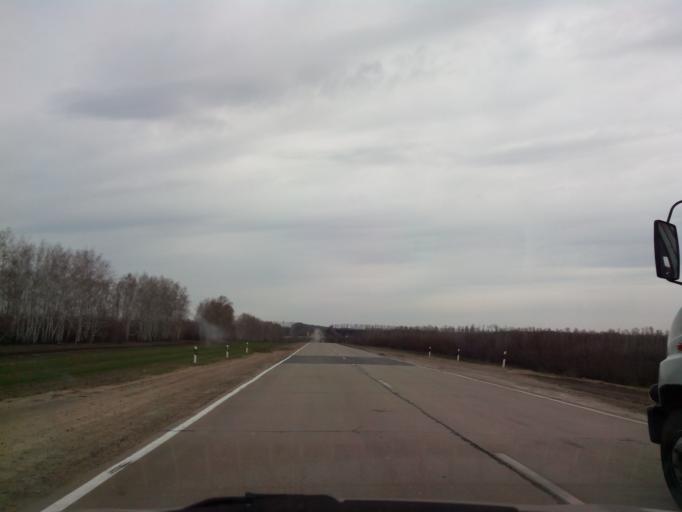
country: RU
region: Tambov
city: Znamenka
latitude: 52.4600
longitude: 41.3673
